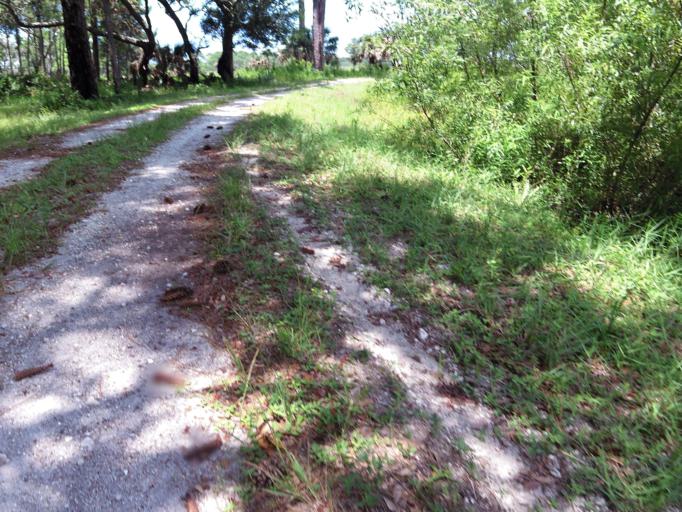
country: US
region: Florida
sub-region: Saint Johns County
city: Villano Beach
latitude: 30.0471
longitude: -81.3442
